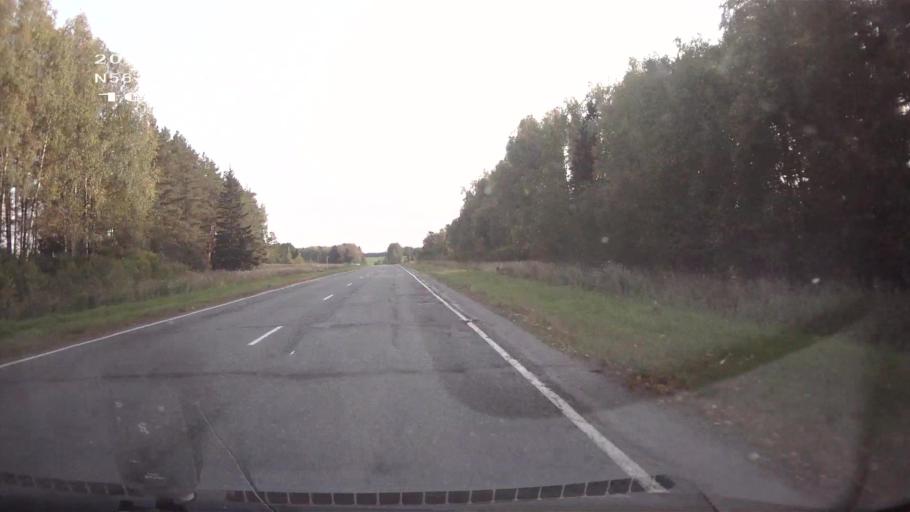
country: RU
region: Mariy-El
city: Kuzhener
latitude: 56.8919
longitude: 48.7519
